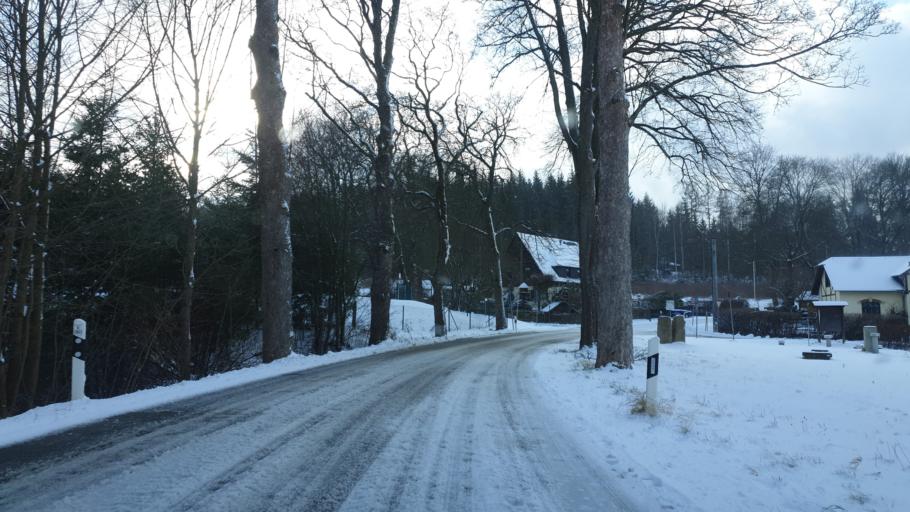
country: DE
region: Saxony
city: Bad Elster
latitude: 50.2742
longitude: 12.2491
